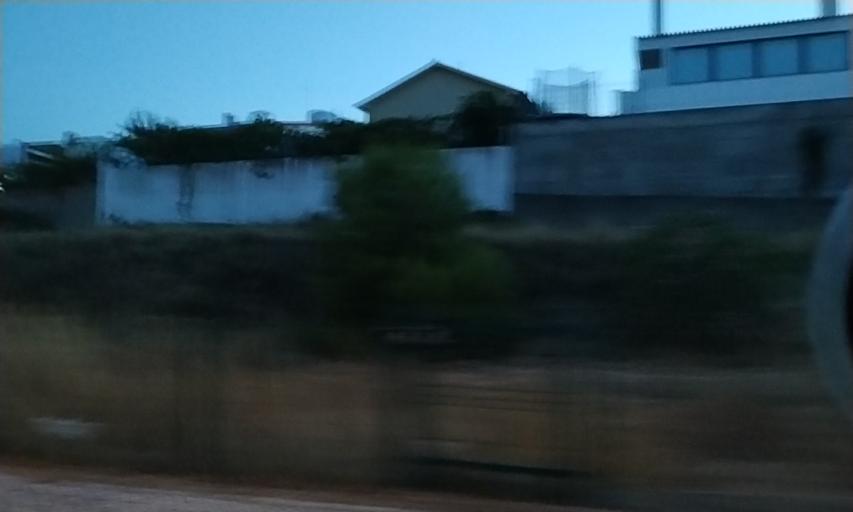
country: PT
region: Setubal
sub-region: Setubal
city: Setubal
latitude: 38.5444
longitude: -8.8962
